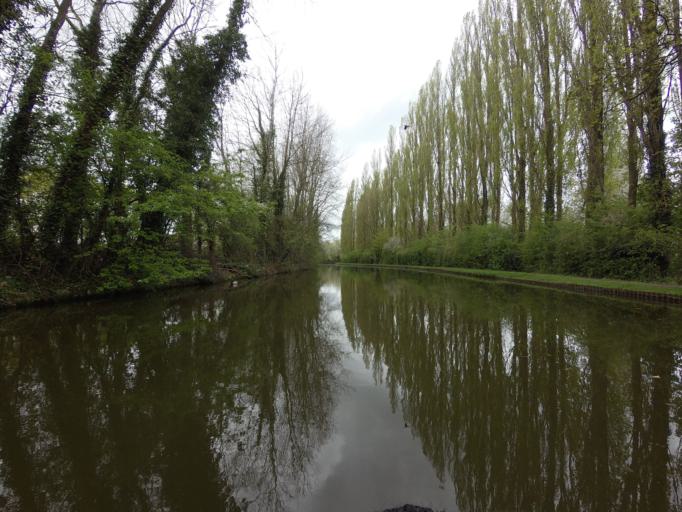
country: GB
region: England
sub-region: Milton Keynes
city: Water Eaton
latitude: 51.9804
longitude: -0.7179
